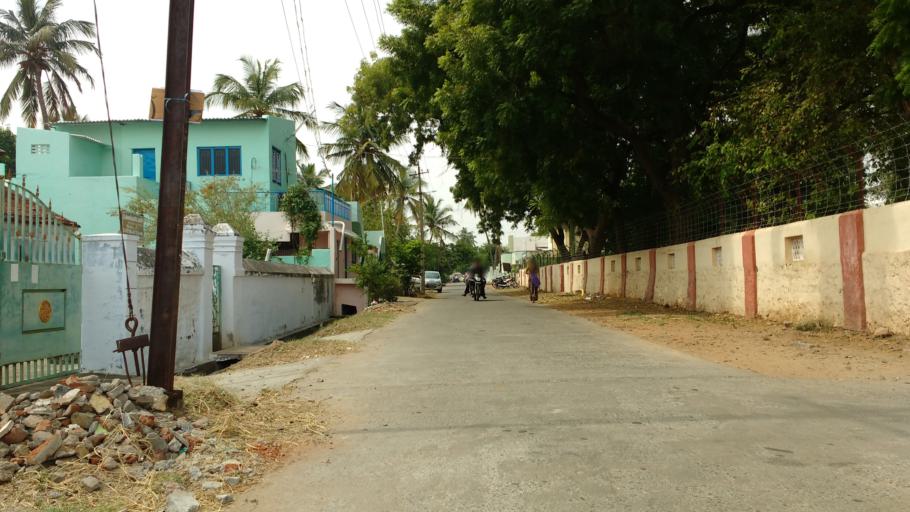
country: IN
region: Tamil Nadu
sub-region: Erode
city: Gobichettipalayam
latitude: 11.4579
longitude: 77.4308
